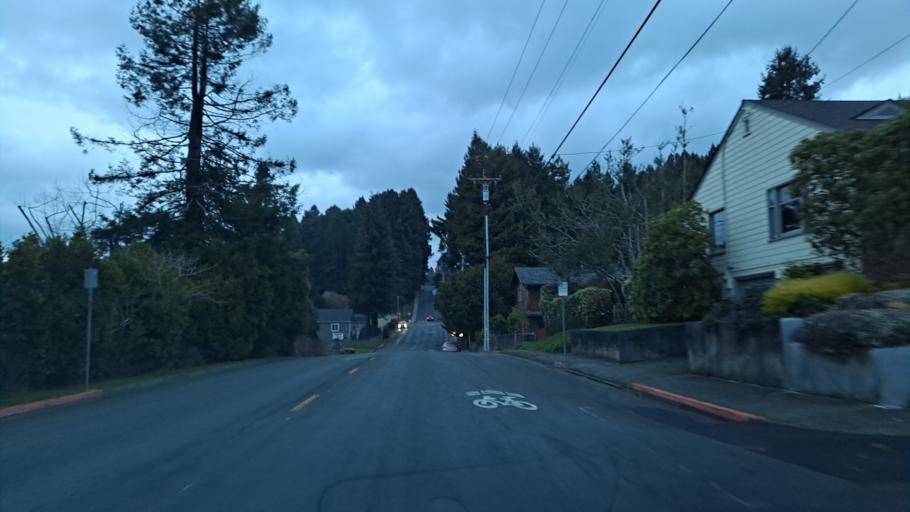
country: US
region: California
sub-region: Humboldt County
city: Arcata
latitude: 40.8696
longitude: -124.0775
